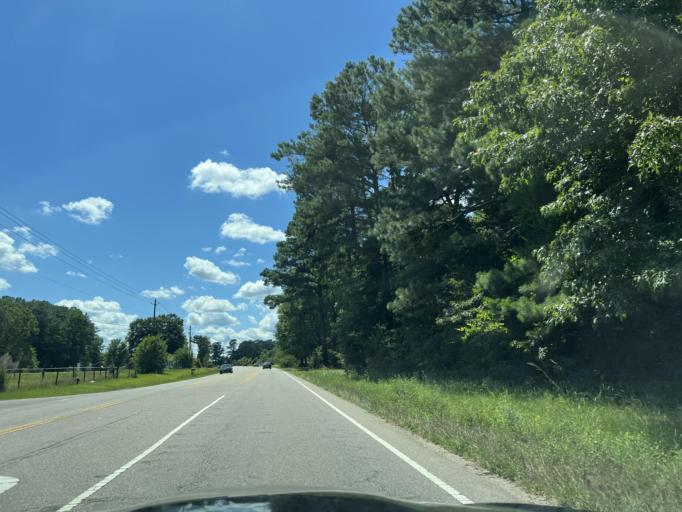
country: US
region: North Carolina
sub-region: Lee County
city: Sanford
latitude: 35.4382
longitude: -79.2092
